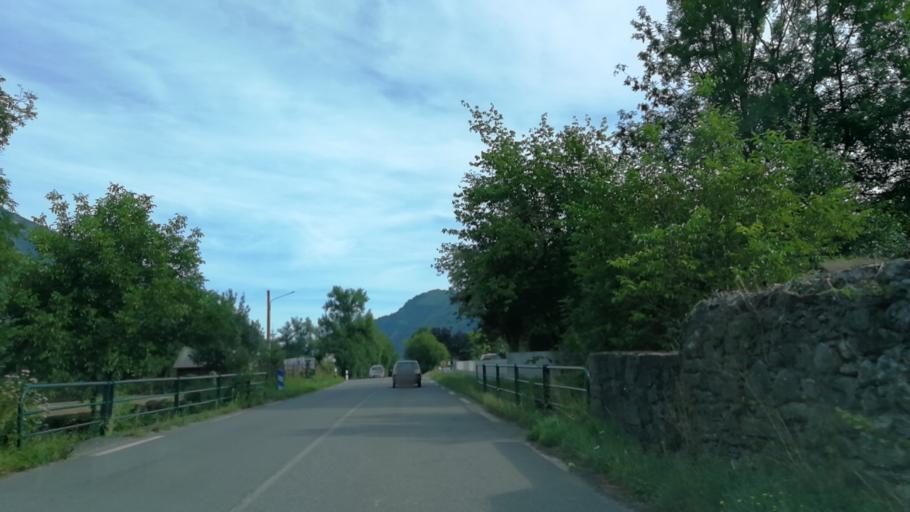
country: FR
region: Aquitaine
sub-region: Departement des Pyrenees-Atlantiques
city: Arette
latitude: 42.9739
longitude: -0.6076
